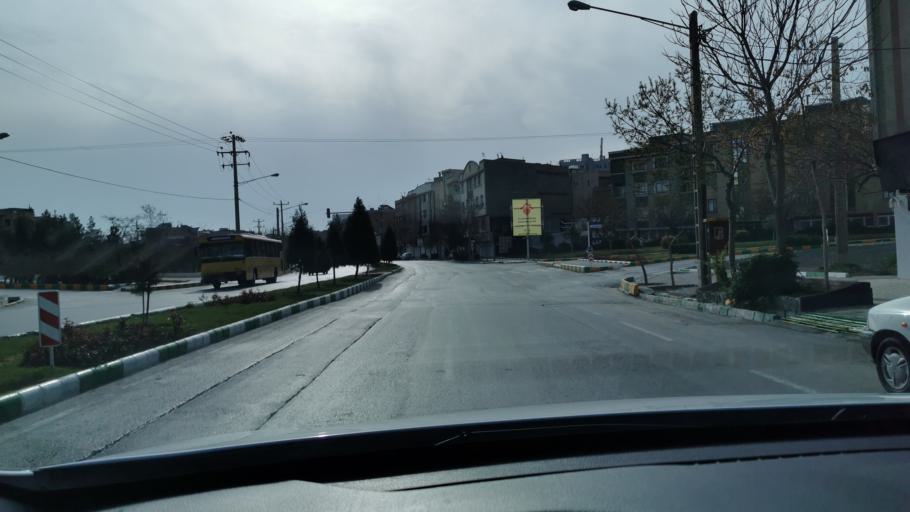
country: IR
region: Razavi Khorasan
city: Mashhad
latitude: 36.3143
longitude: 59.5115
